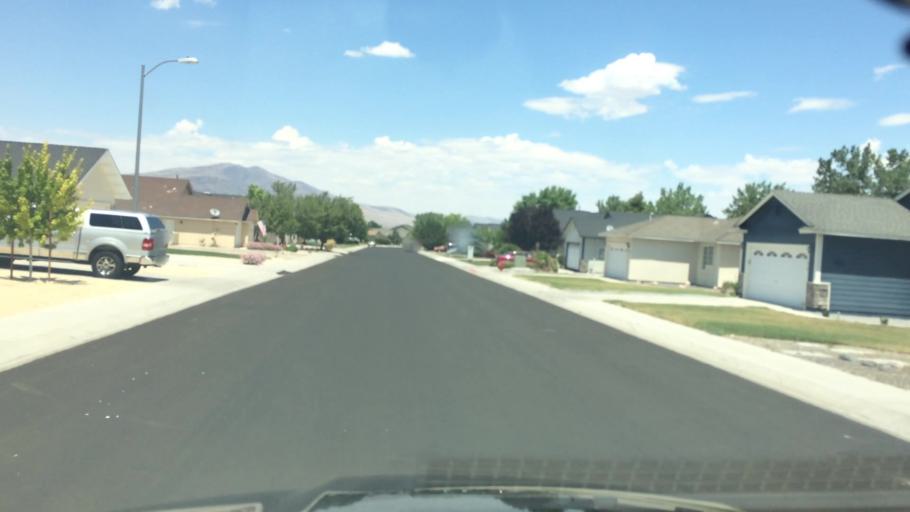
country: US
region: Nevada
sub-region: Lyon County
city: Fernley
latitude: 39.5850
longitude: -119.1411
